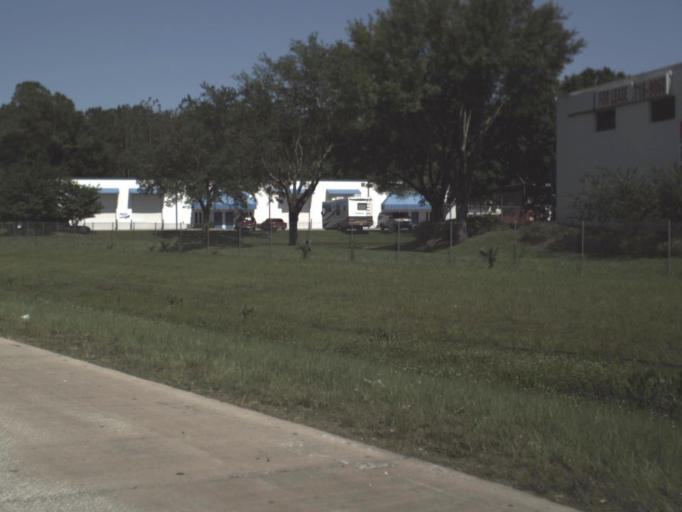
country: US
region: Florida
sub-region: Duval County
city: Jacksonville
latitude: 30.3163
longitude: -81.7385
